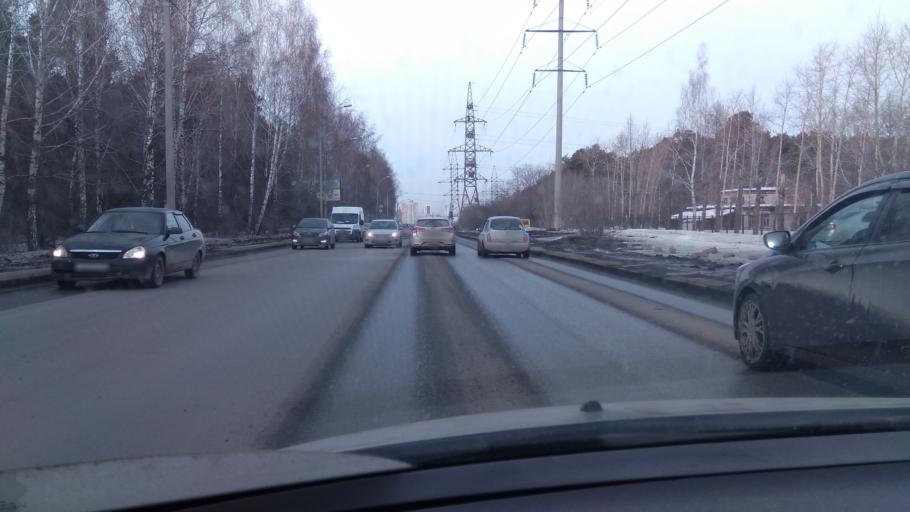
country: RU
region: Sverdlovsk
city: Sovkhoznyy
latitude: 56.7825
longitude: 60.5982
